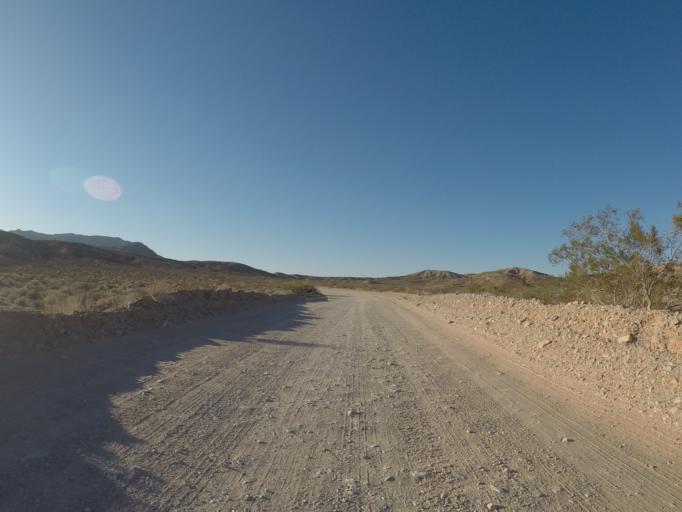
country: US
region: Nevada
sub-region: Clark County
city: Moapa Valley
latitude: 36.3866
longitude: -114.4138
